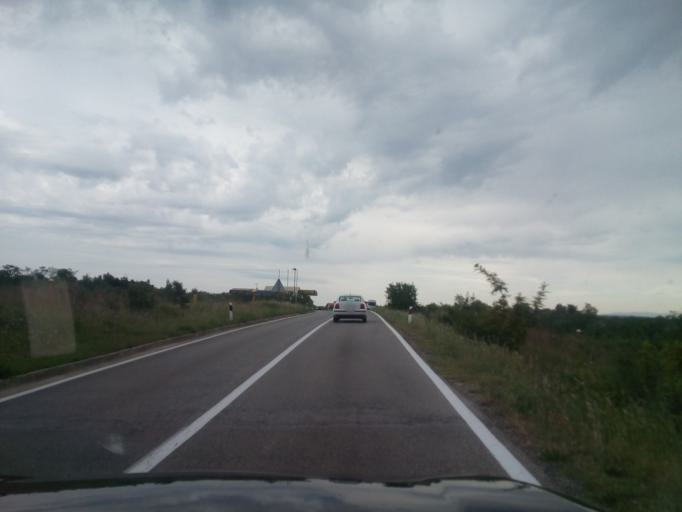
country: HR
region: Sibensko-Kniniska
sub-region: Grad Sibenik
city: Sibenik
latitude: 43.7754
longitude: 15.9582
